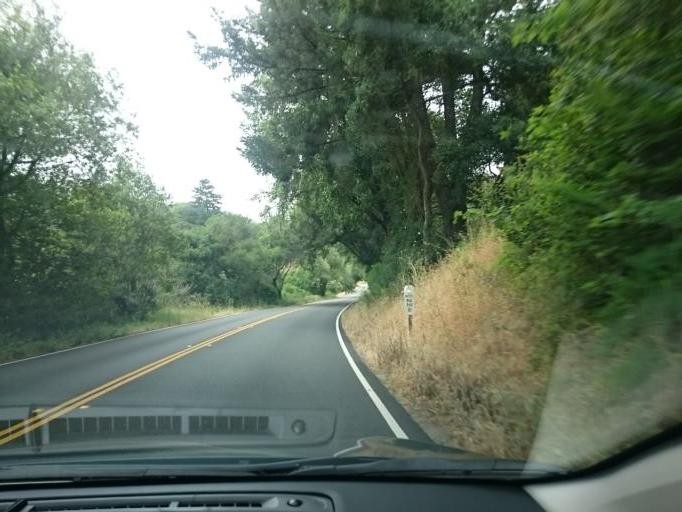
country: US
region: California
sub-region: Marin County
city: Lagunitas-Forest Knolls
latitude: 37.9930
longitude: -122.7525
